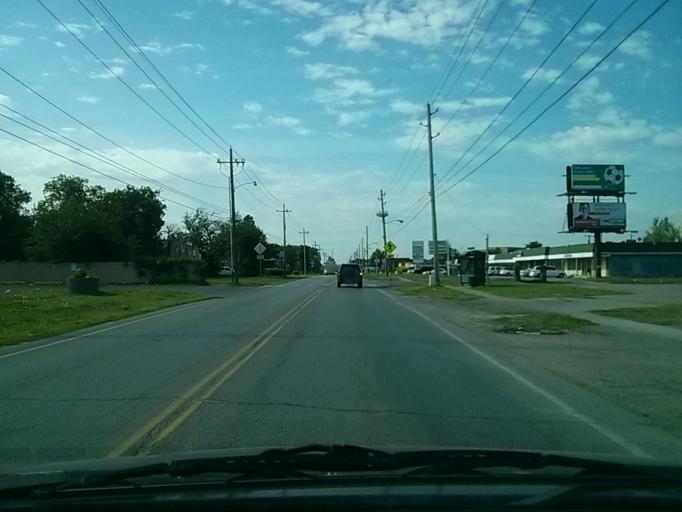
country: US
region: Oklahoma
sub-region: Tulsa County
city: Jenks
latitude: 36.0729
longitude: -95.9758
